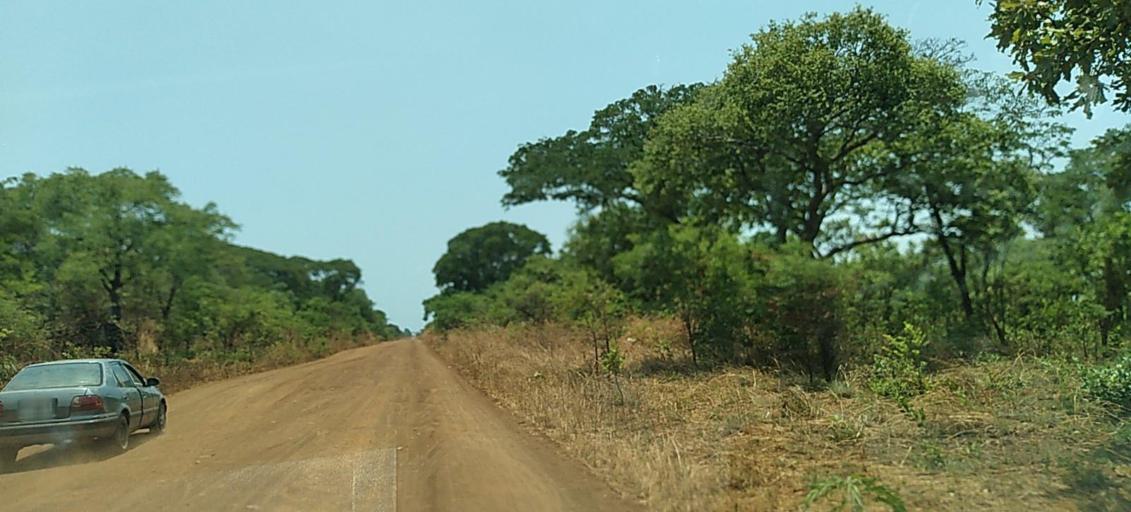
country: ZM
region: Copperbelt
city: Mpongwe
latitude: -13.6892
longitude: 27.8613
